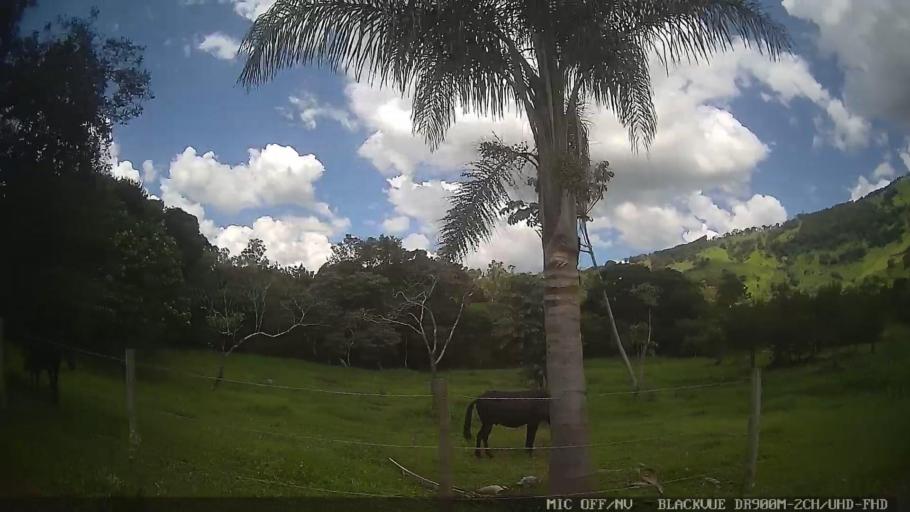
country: BR
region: Minas Gerais
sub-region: Extrema
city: Extrema
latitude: -22.8602
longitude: -46.2817
